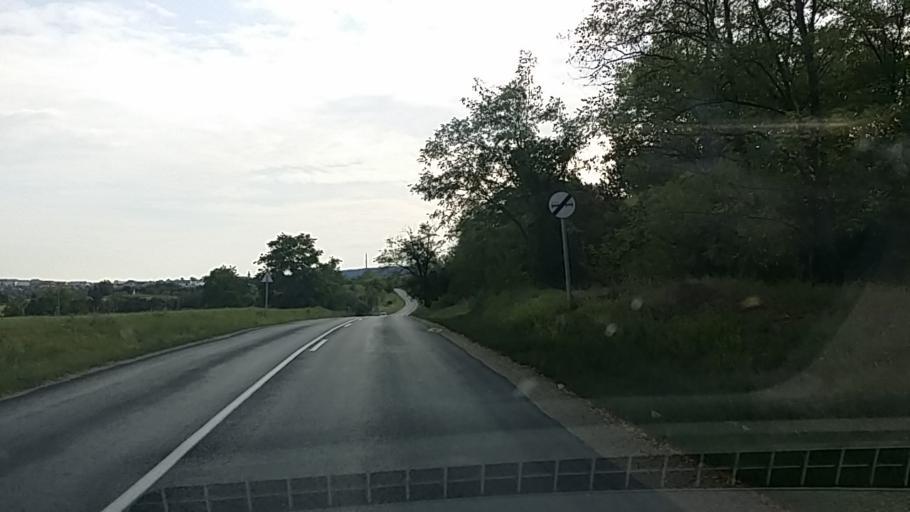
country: HU
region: Gyor-Moson-Sopron
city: Sopron
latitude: 47.7140
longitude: 16.6128
